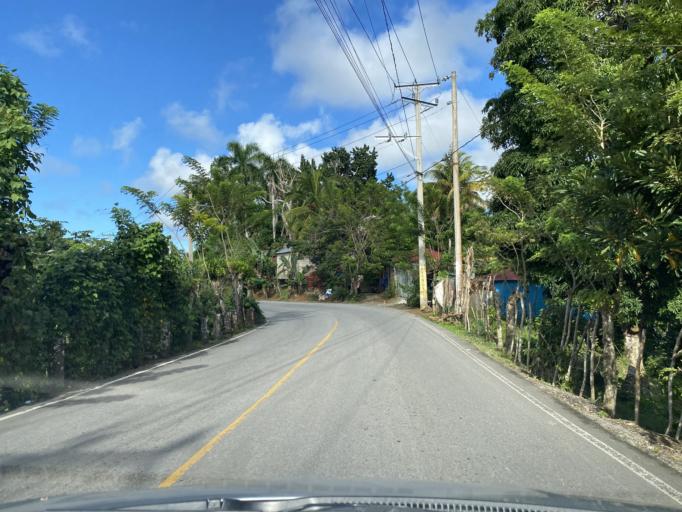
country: DO
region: Samana
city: Las Terrenas
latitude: 19.2648
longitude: -69.5652
